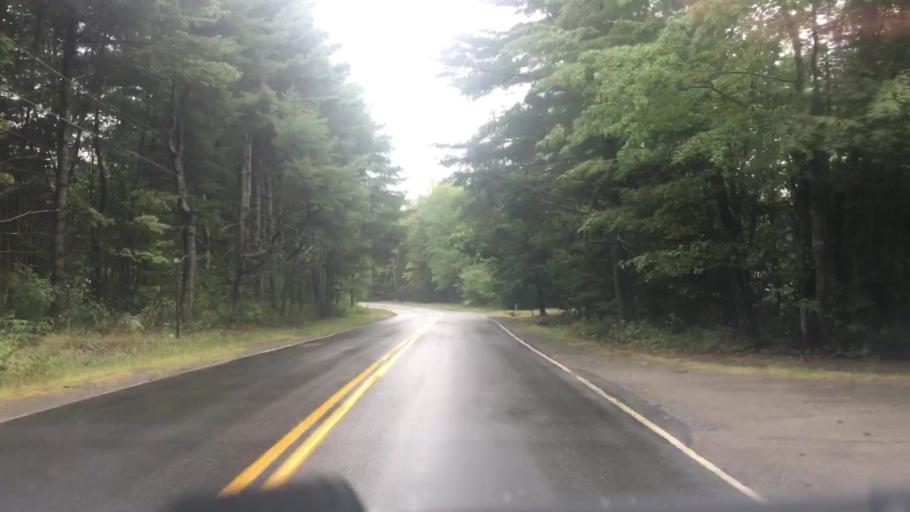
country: US
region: Maine
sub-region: Penobscot County
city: Hudson
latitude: 44.9878
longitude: -68.7972
